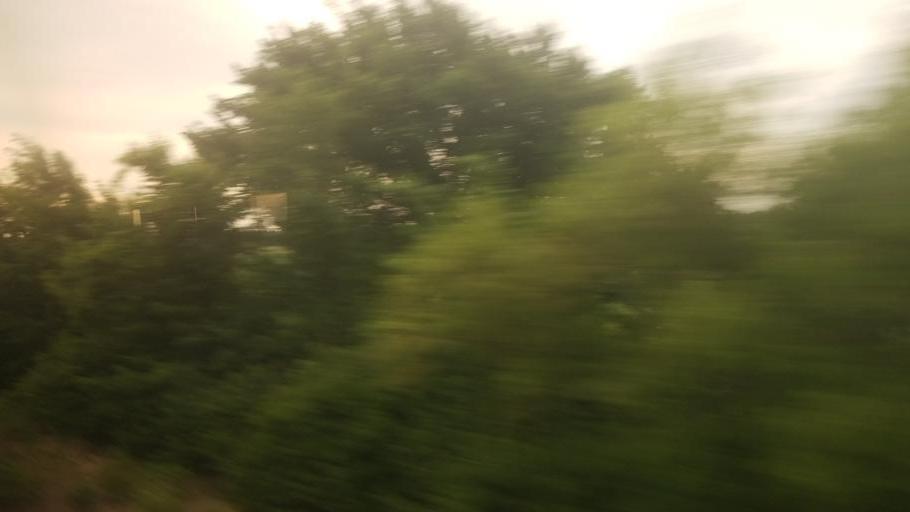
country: US
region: Kansas
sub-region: Chase County
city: Cottonwood Falls
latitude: 38.3849
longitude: -96.4921
